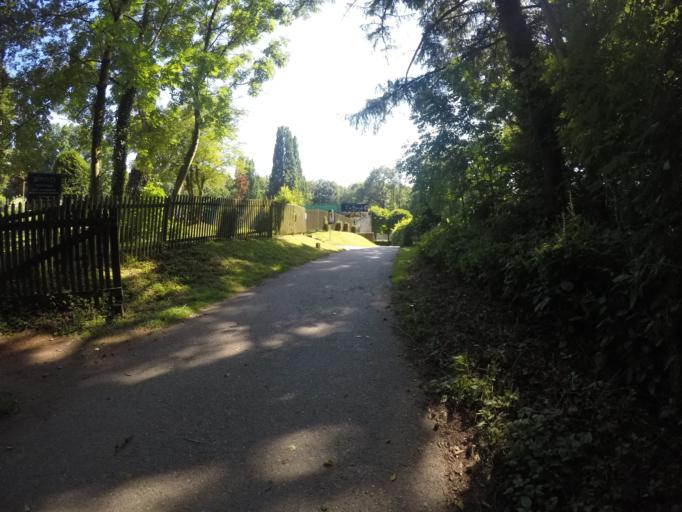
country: DE
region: North Rhine-Westphalia
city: Bad Oeynhausen
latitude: 52.1957
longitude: 8.7897
